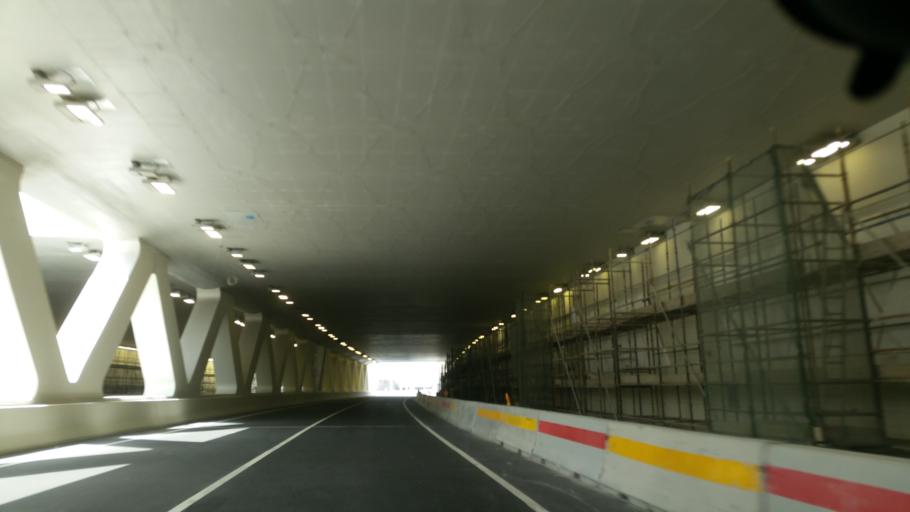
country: QA
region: Baladiyat Umm Salal
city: Umm Salal Muhammad
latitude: 25.4252
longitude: 51.5079
